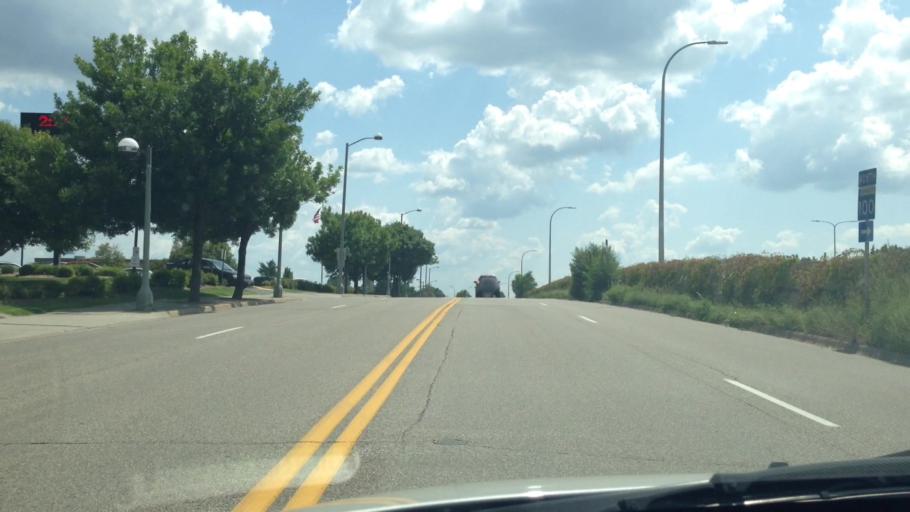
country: US
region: Minnesota
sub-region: Hennepin County
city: Saint Louis Park
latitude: 44.9344
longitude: -93.3495
